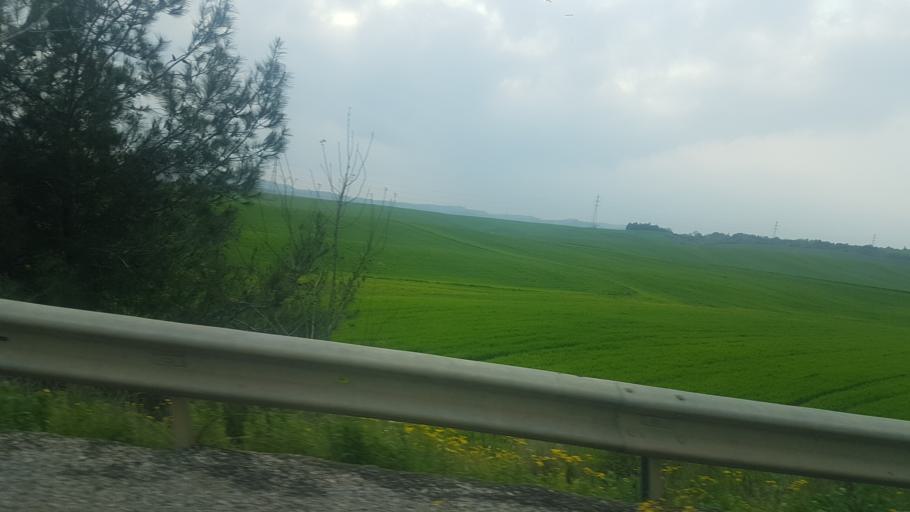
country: TR
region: Mersin
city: Yenice
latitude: 37.0700
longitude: 35.1722
